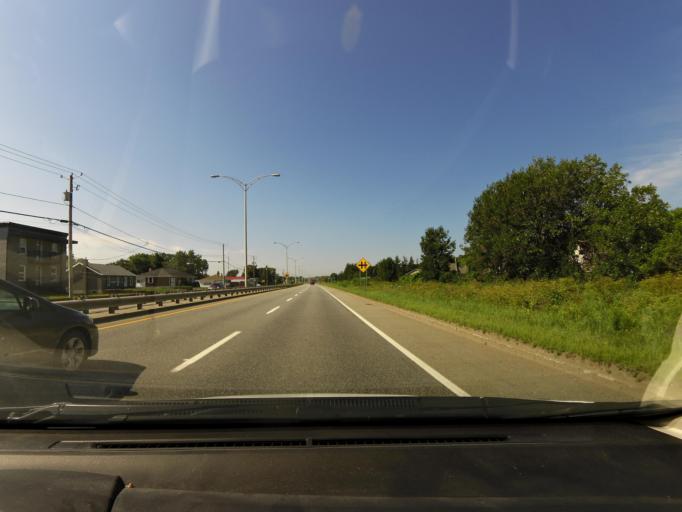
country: CA
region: Quebec
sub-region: Capitale-Nationale
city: Chateau-Richer
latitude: 46.9630
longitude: -71.0284
